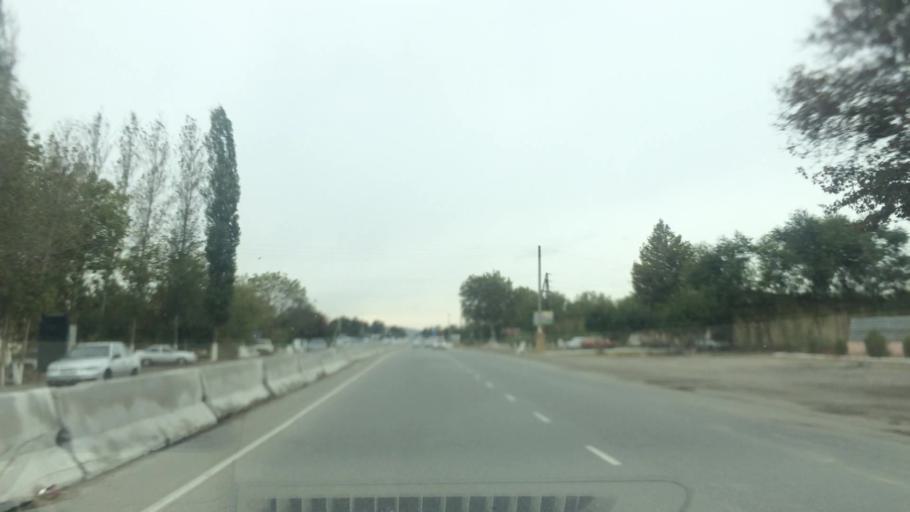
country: UZ
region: Samarqand
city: Jomboy
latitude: 39.7168
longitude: 67.1089
